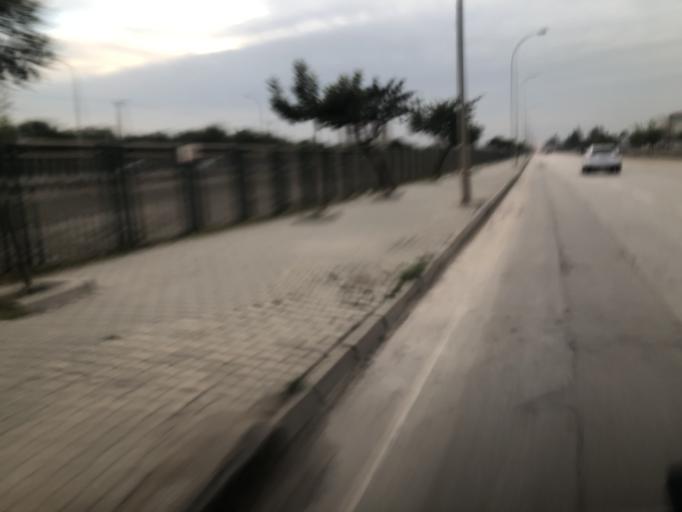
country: TR
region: Adana
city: Seyhan
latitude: 37.0098
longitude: 35.2630
